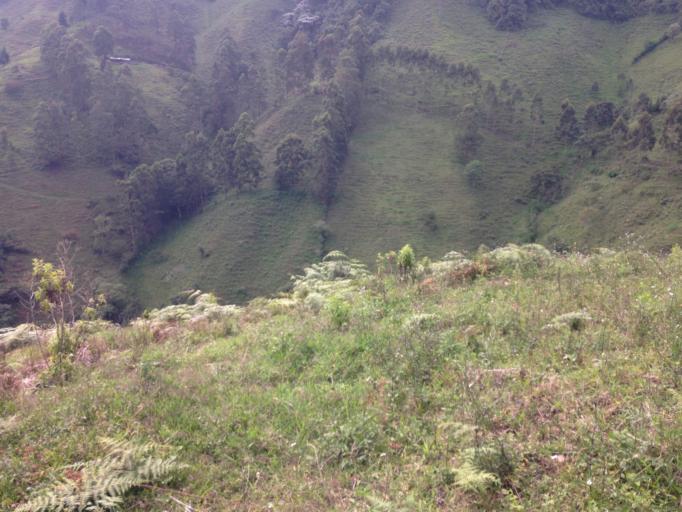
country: CO
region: Valle del Cauca
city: Ginebra
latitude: 3.7683
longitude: -76.1850
